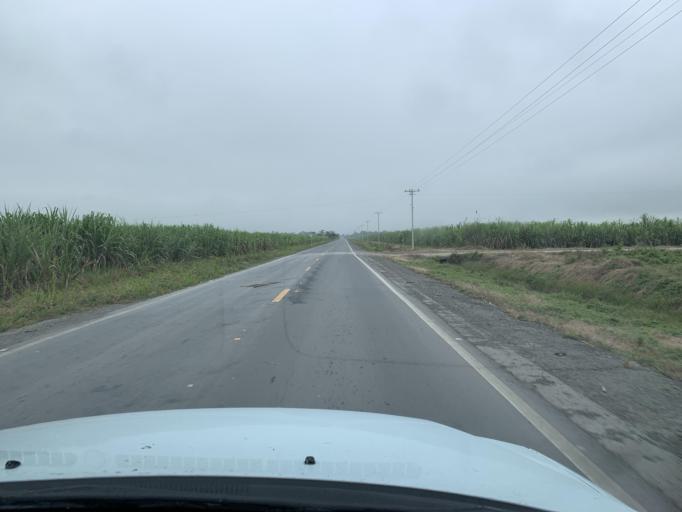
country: EC
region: Guayas
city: Coronel Marcelino Mariduena
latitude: -2.3227
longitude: -79.5199
